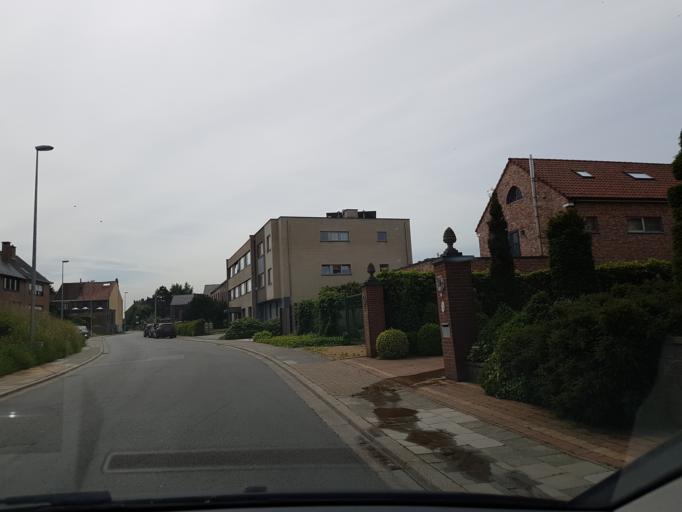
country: BE
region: Flanders
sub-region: Provincie Vlaams-Brabant
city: Asse
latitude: 50.9022
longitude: 4.2103
